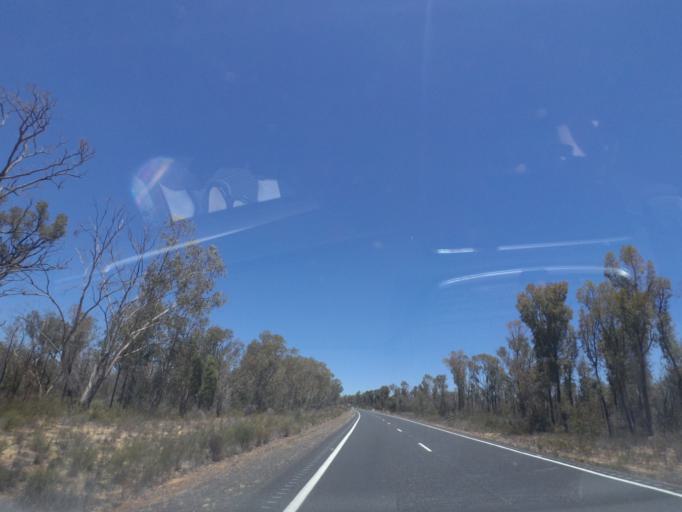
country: AU
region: New South Wales
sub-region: Warrumbungle Shire
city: Coonabarabran
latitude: -30.9436
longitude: 149.4229
